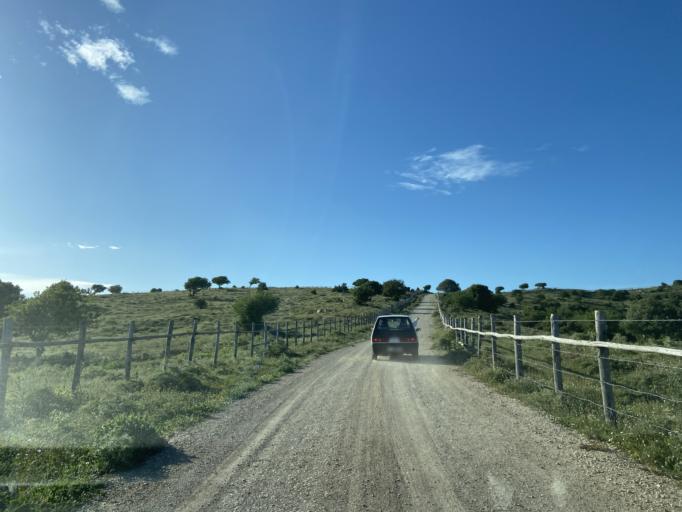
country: IT
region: Latium
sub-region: Citta metropolitana di Roma Capitale
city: Santa Marinella
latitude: 42.0857
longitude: 11.8525
